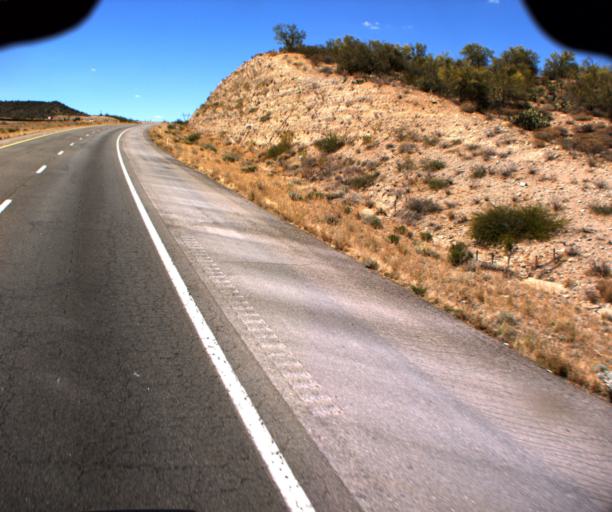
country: US
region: Arizona
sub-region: Yavapai County
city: Bagdad
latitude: 34.4323
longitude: -113.2531
